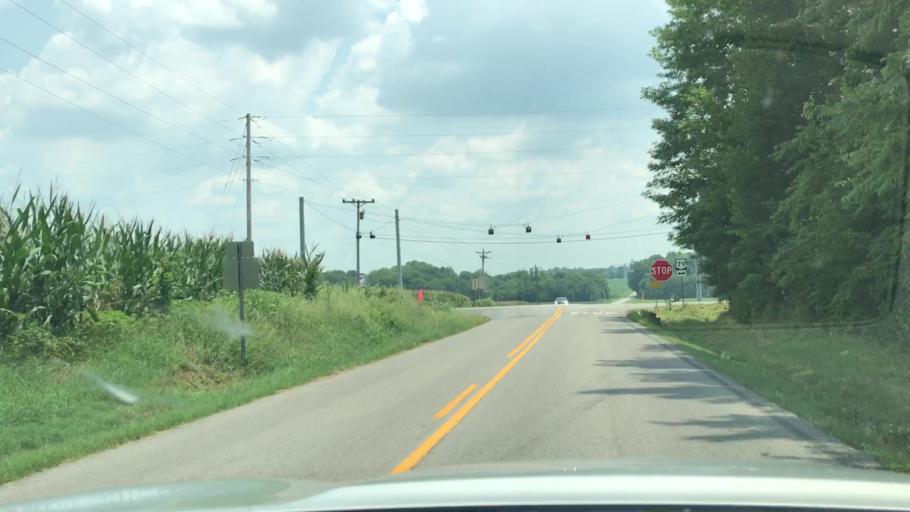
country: US
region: Kentucky
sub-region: Todd County
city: Elkton
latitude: 36.7255
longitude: -87.0873
